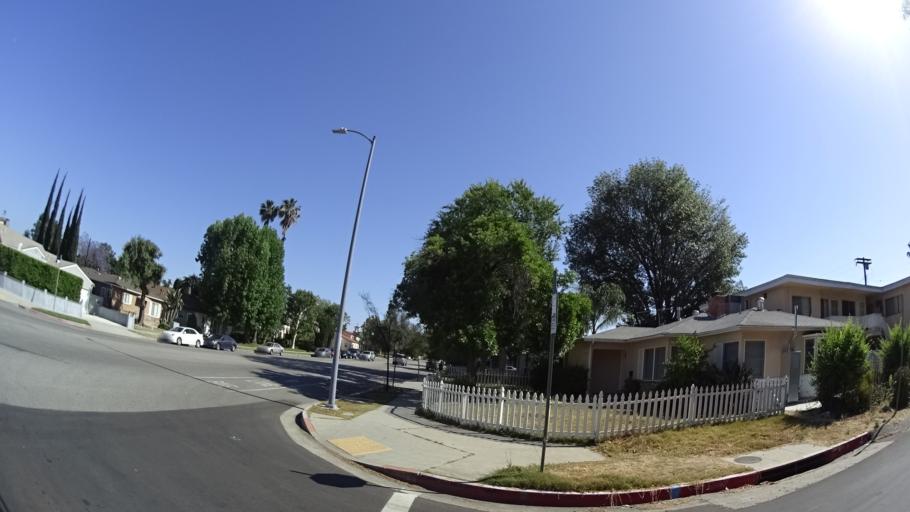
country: US
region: California
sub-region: Los Angeles County
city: North Hollywood
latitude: 34.1631
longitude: -118.3879
